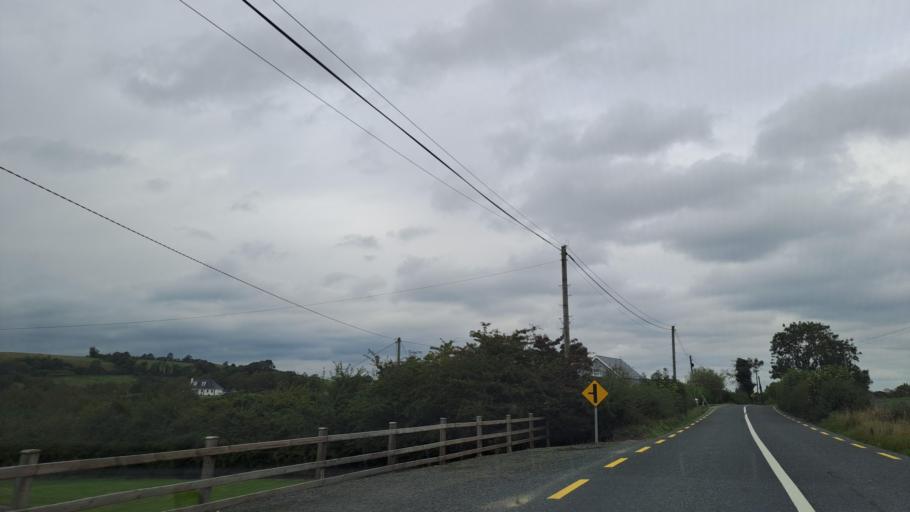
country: IE
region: Ulster
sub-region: An Cabhan
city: Bailieborough
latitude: 53.9519
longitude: -6.9518
